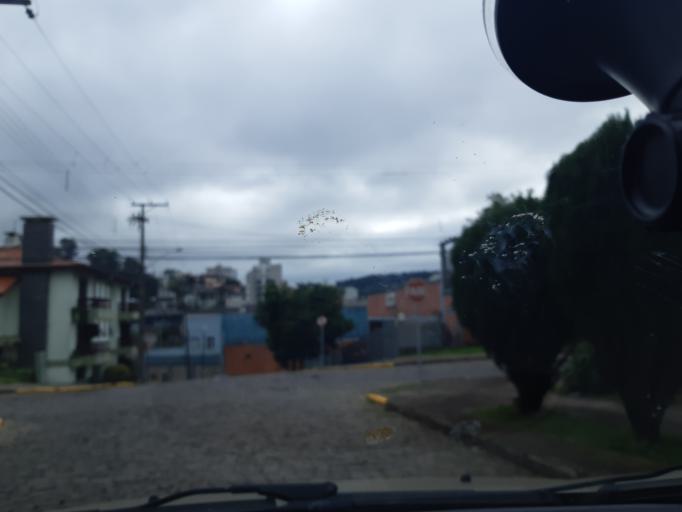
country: BR
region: Rio Grande do Sul
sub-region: Caxias Do Sul
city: Caxias do Sul
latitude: -29.1554
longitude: -51.2066
